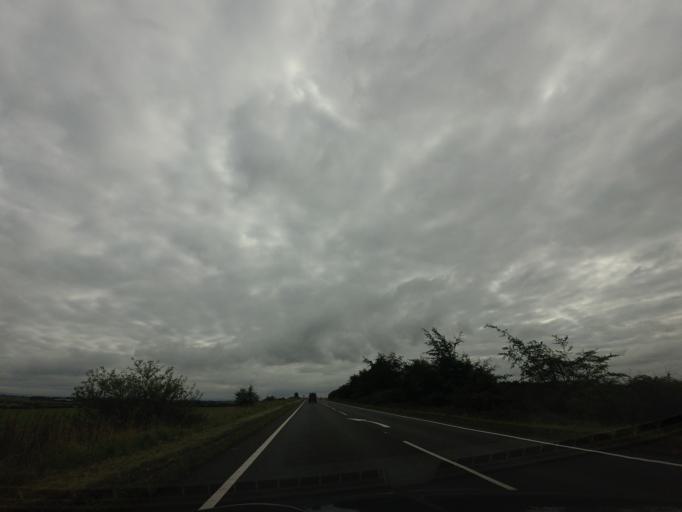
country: GB
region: Scotland
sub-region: Dumfries and Galloway
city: Gretna
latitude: 54.9930
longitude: -3.1243
